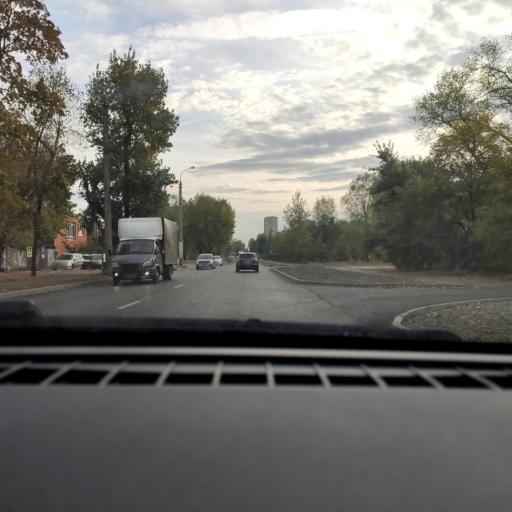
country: RU
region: Voronezj
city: Voronezh
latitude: 51.6603
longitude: 39.2503
